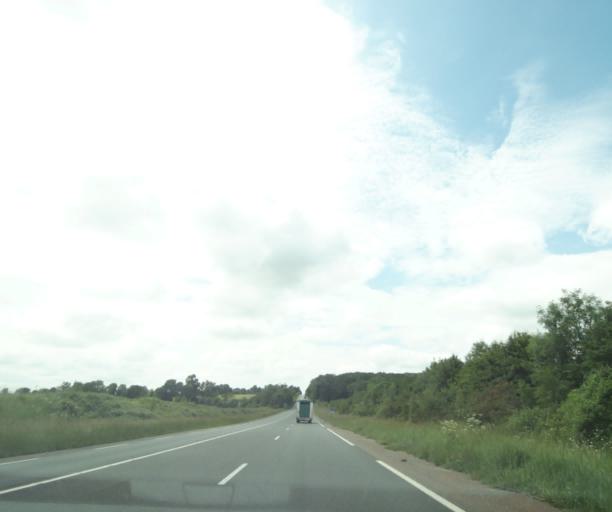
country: FR
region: Poitou-Charentes
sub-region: Departement des Deux-Sevres
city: Saint-Pardoux
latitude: 46.5128
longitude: -0.3316
